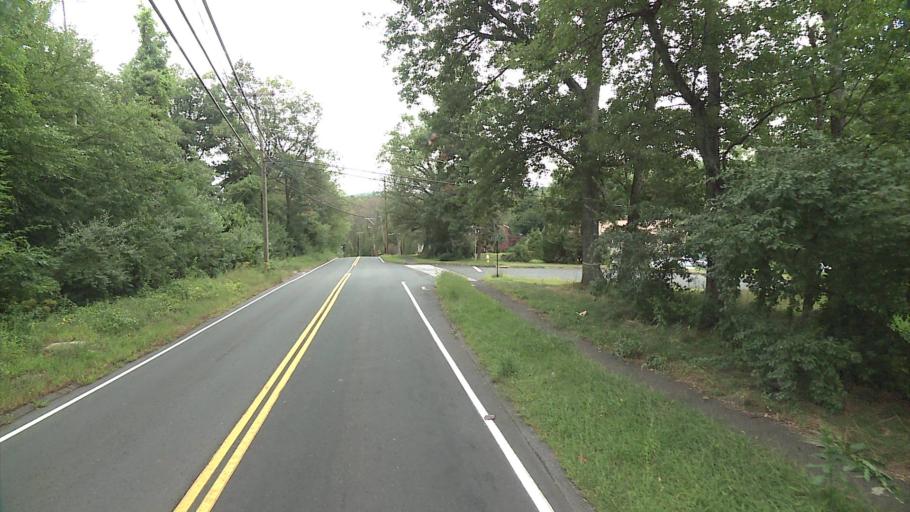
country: US
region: Connecticut
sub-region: Tolland County
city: Rockville
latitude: 41.8201
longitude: -72.4634
